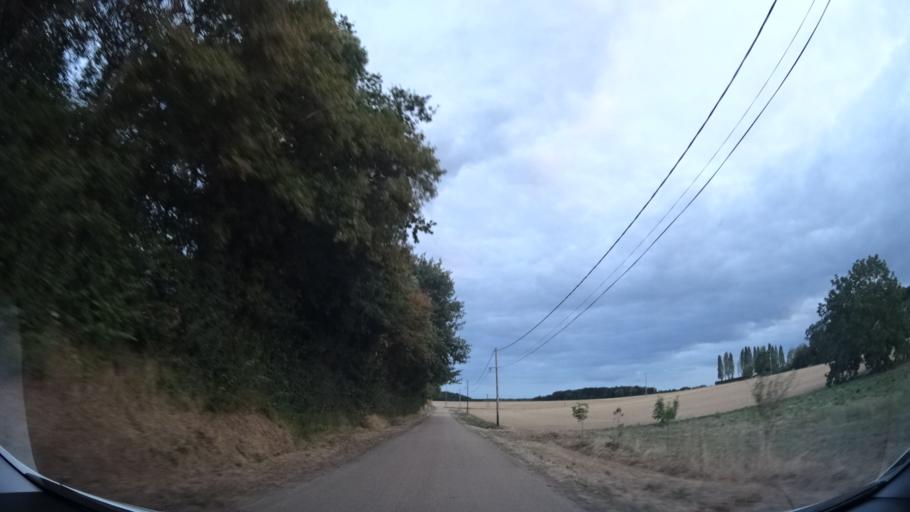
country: FR
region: Bourgogne
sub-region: Departement de l'Yonne
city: Cezy
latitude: 47.9347
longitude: 3.2760
